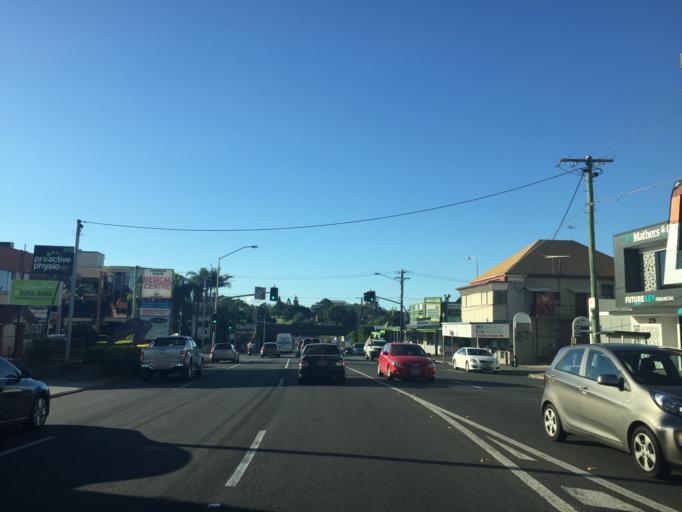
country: AU
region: Queensland
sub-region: Brisbane
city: Windsor
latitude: -27.4359
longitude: 153.0314
